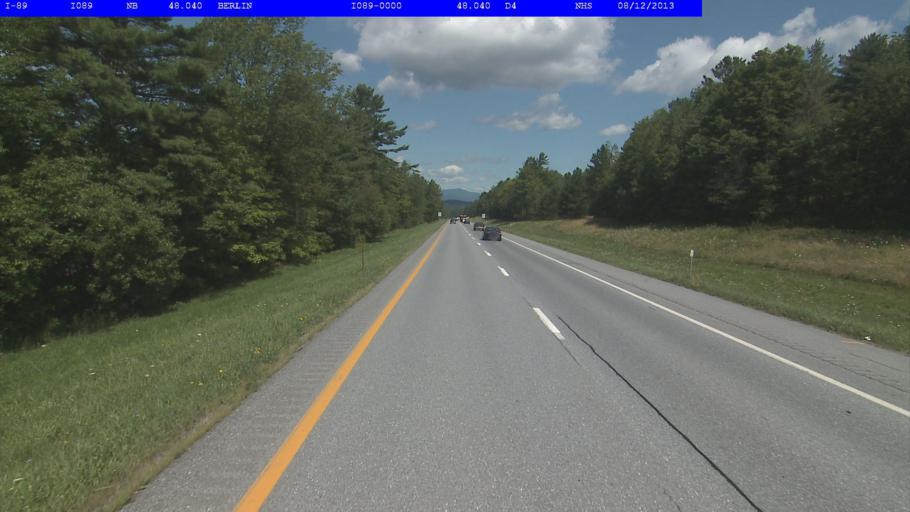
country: US
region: Vermont
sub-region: Washington County
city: South Barre
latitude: 44.1838
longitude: -72.5758
